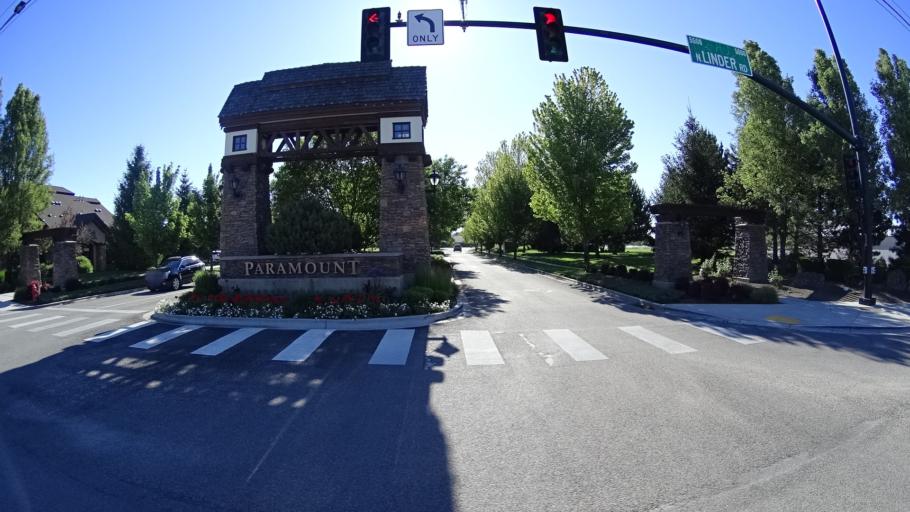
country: US
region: Idaho
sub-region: Ada County
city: Meridian
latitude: 43.6558
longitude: -116.4137
